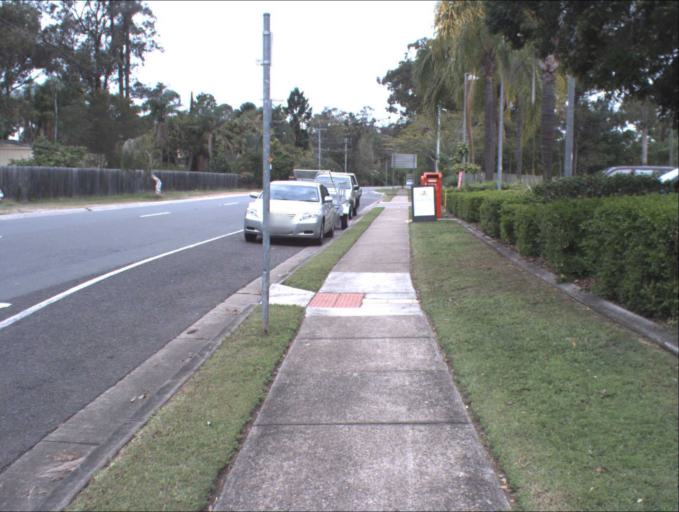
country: AU
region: Queensland
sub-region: Brisbane
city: Forest Lake
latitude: -27.6570
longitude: 153.0074
